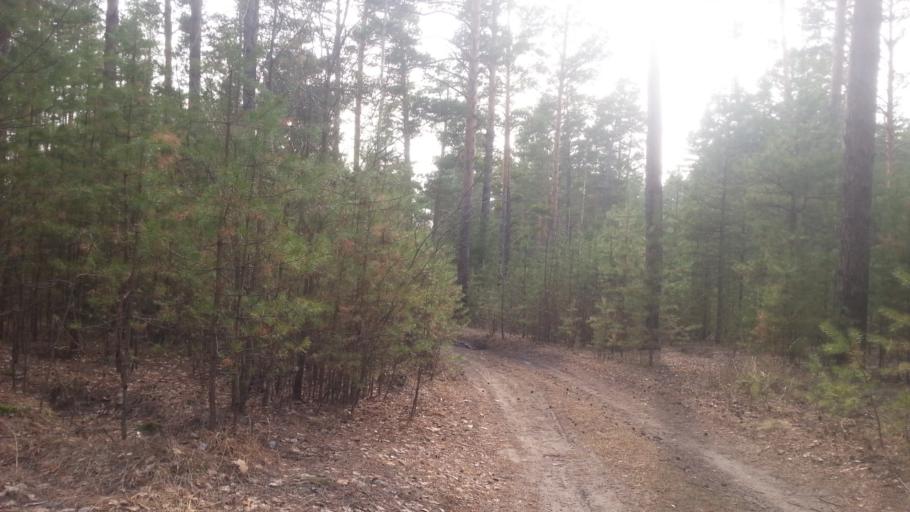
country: RU
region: Altai Krai
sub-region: Gorod Barnaulskiy
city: Barnaul
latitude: 53.3250
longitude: 83.7197
